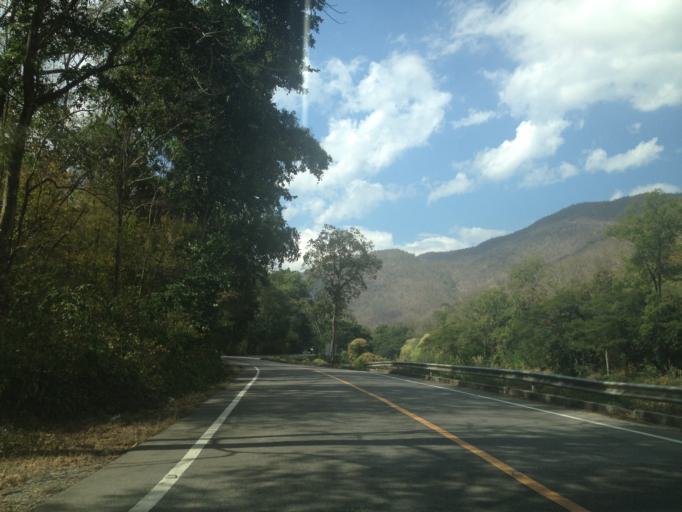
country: TH
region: Chiang Mai
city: Hot
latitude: 18.2341
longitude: 98.5410
